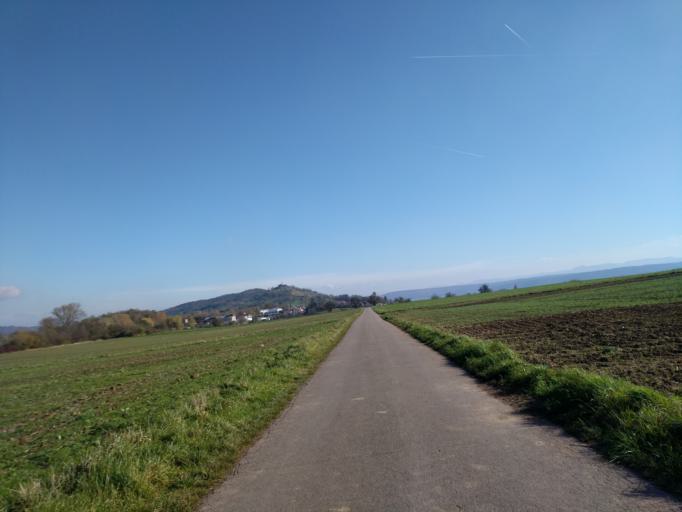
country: DE
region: Baden-Wuerttemberg
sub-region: Tuebingen Region
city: Rottenburg
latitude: 48.5075
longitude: 8.9539
